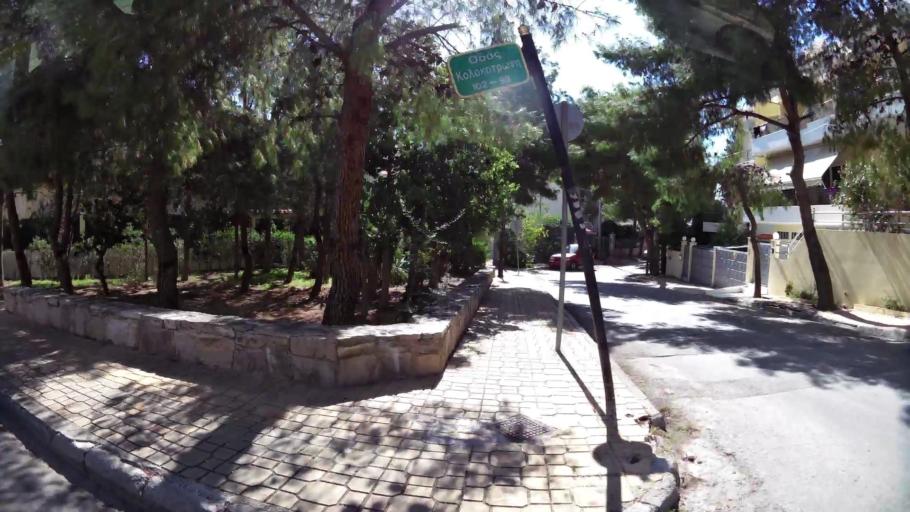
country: GR
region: Attica
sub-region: Nomarchia Anatolikis Attikis
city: Voula
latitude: 37.8399
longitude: 23.7844
